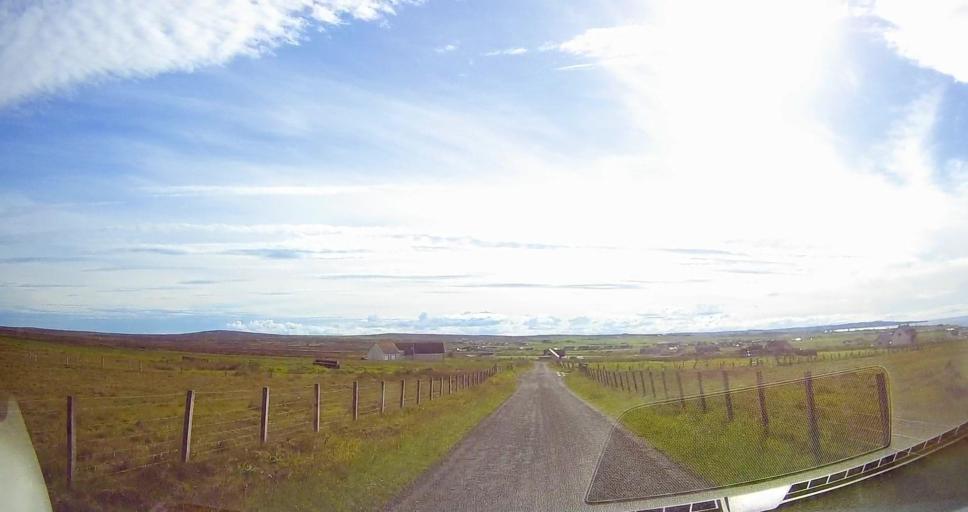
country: GB
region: Scotland
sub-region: Highland
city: Wick
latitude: 58.6381
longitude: -3.0443
